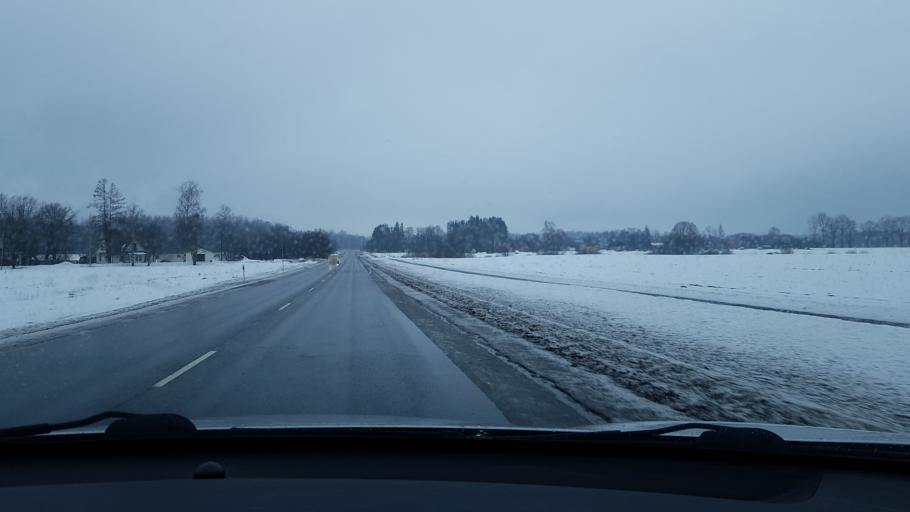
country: EE
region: Jaervamaa
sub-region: Tueri vald
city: Tueri
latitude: 58.8154
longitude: 25.3986
